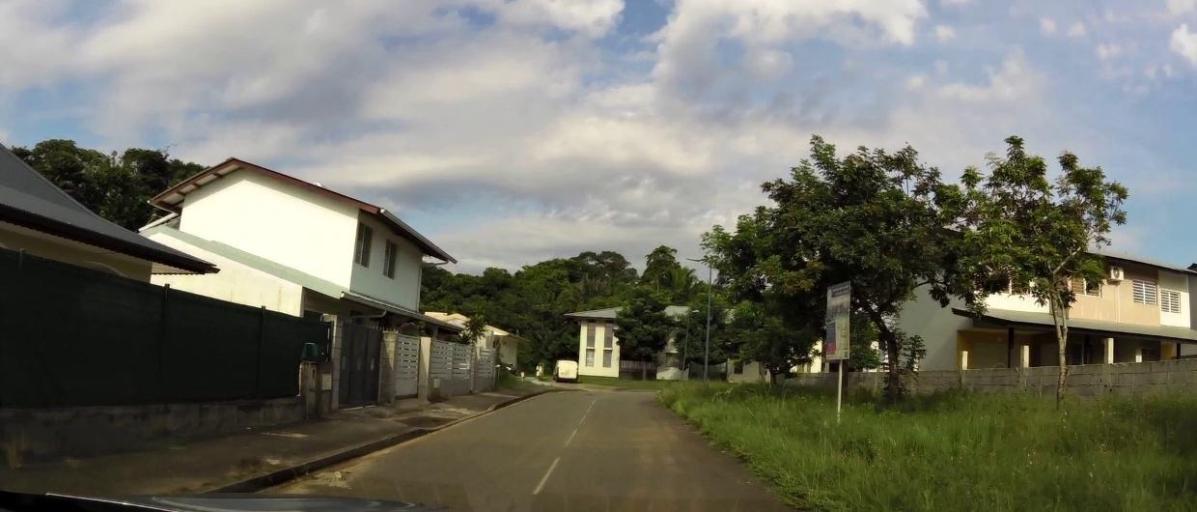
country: GF
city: Macouria
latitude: 4.9217
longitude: -52.4173
